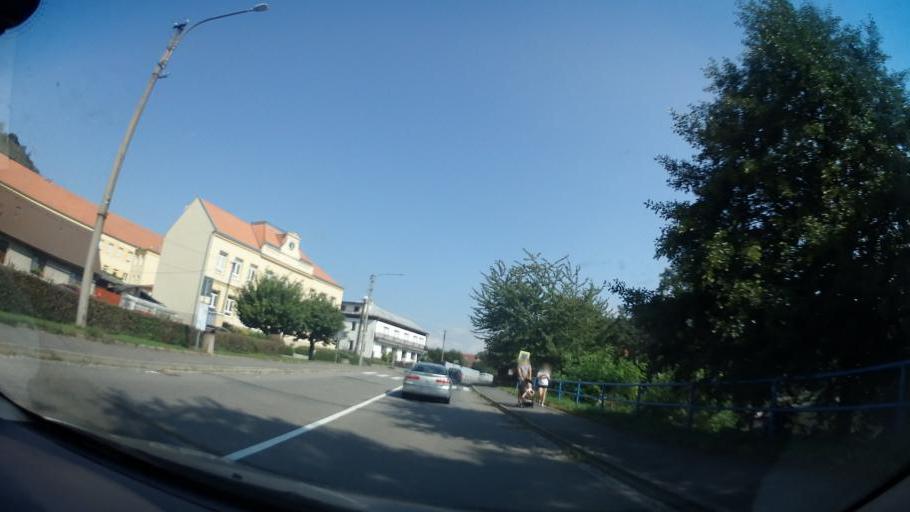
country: CZ
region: South Moravian
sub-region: Okres Brno-Venkov
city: Nedvedice
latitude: 49.4556
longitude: 16.3322
